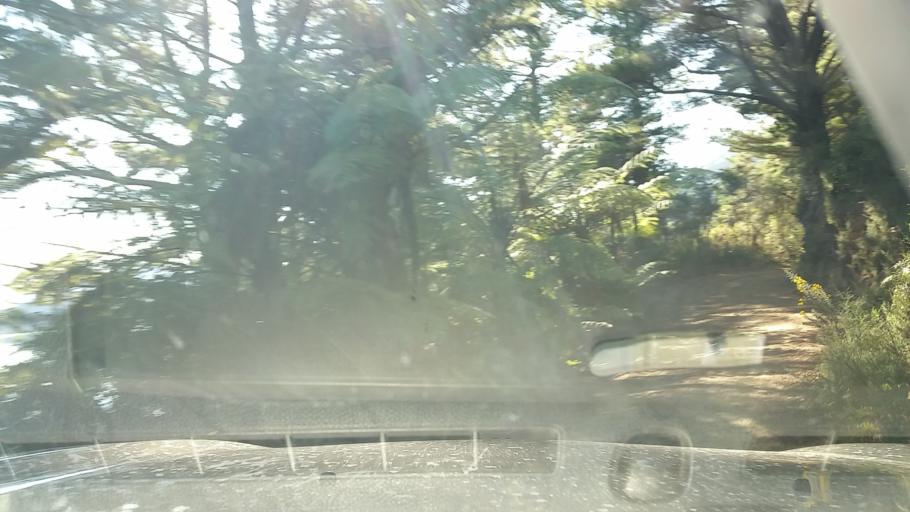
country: NZ
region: Marlborough
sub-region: Marlborough District
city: Picton
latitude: -41.1203
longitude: 173.9903
